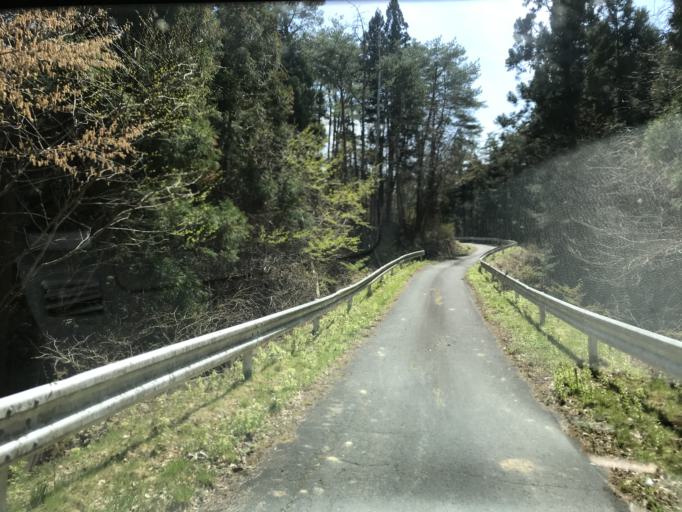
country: JP
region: Iwate
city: Ichinoseki
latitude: 38.8369
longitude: 141.2885
